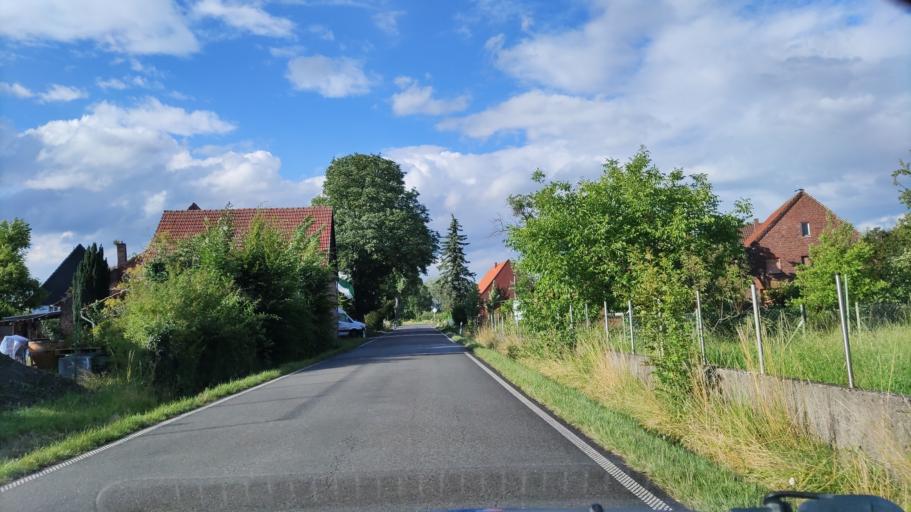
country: DE
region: North Rhine-Westphalia
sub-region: Regierungsbezirk Arnsberg
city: Welver
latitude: 51.6480
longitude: 7.9647
